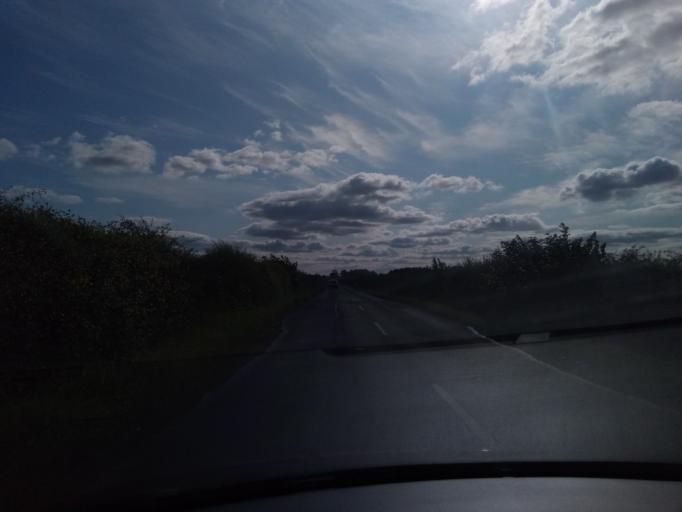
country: GB
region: Scotland
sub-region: The Scottish Borders
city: Allanton
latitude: 55.7485
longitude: -2.1587
